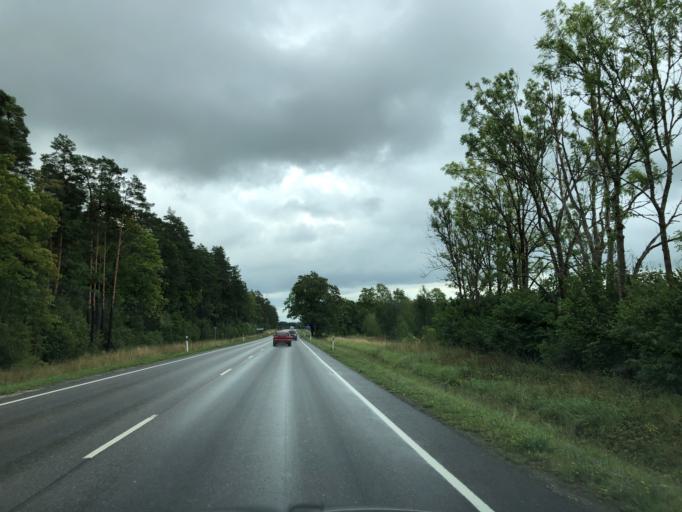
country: EE
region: Laeaene
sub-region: Ridala Parish
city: Uuemoisa
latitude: 58.9590
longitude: 23.7148
